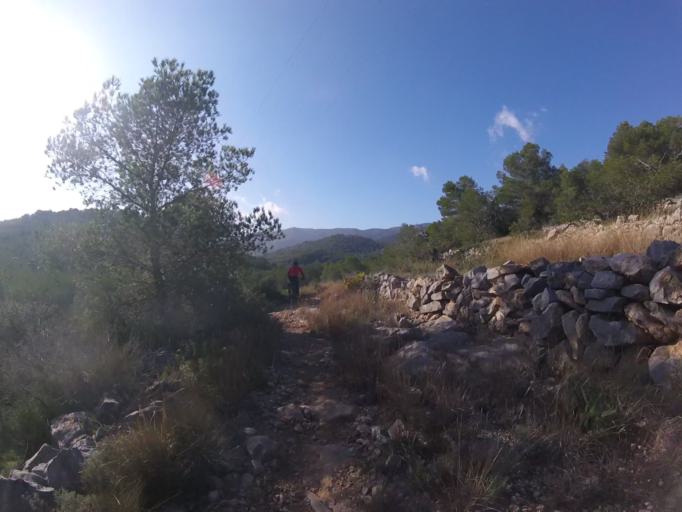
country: ES
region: Valencia
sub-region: Provincia de Castello
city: Santa Magdalena de Pulpis
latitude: 40.2983
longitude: 0.3291
